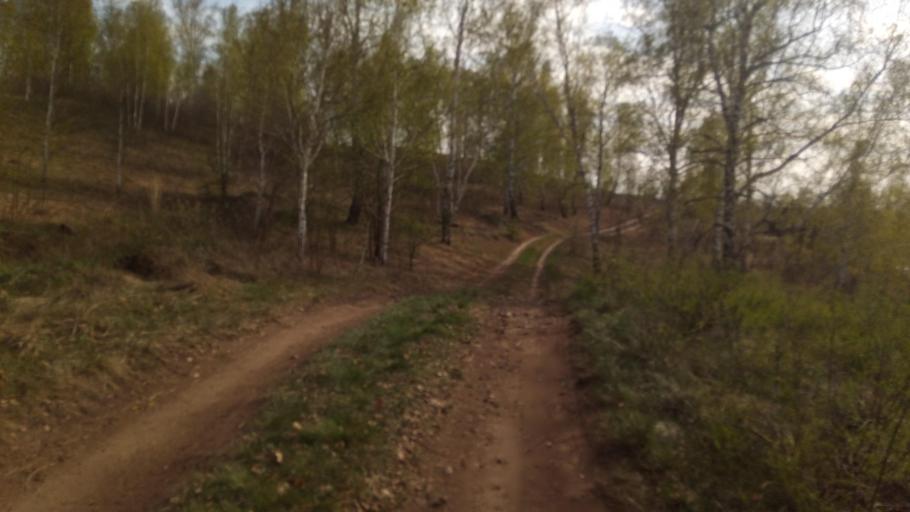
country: RU
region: Chelyabinsk
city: Poletayevo
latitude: 55.0305
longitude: 61.0737
